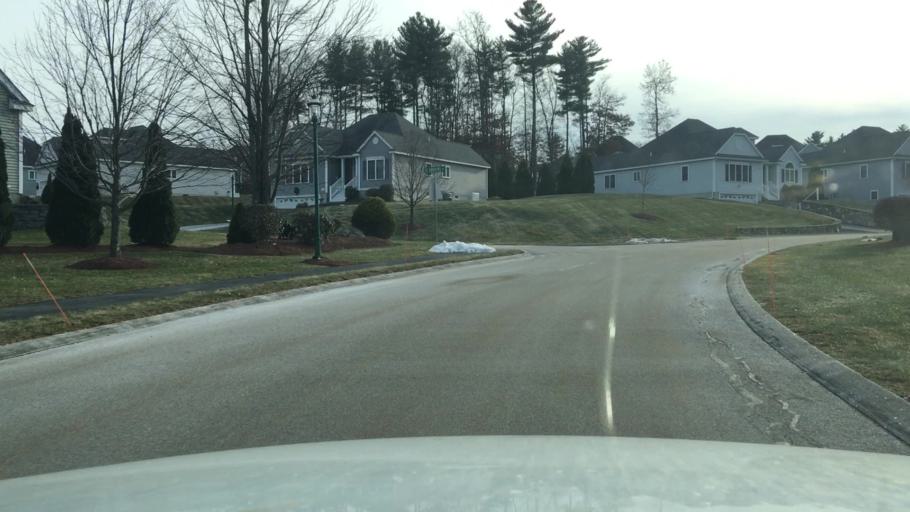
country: US
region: New Hampshire
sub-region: Rockingham County
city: Londonderry
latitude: 42.8896
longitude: -71.4151
